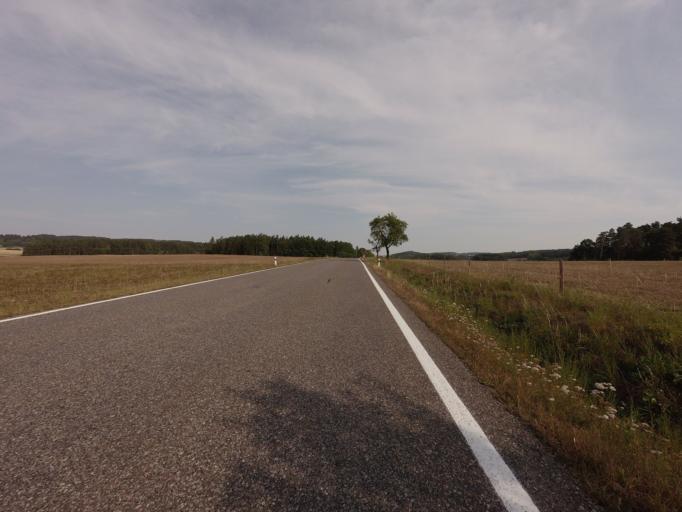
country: CZ
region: Jihocesky
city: Milevsko
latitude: 49.4857
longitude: 14.3656
